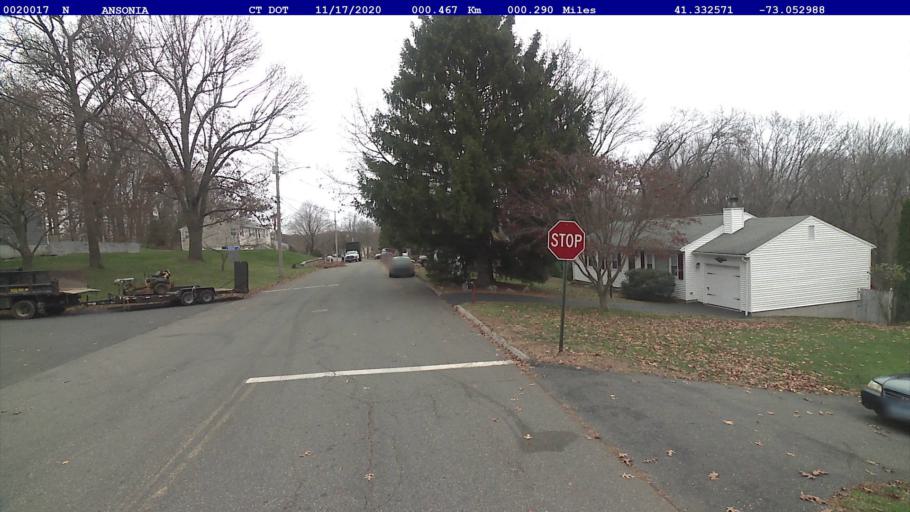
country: US
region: Connecticut
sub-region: New Haven County
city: Ansonia
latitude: 41.3326
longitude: -73.0530
